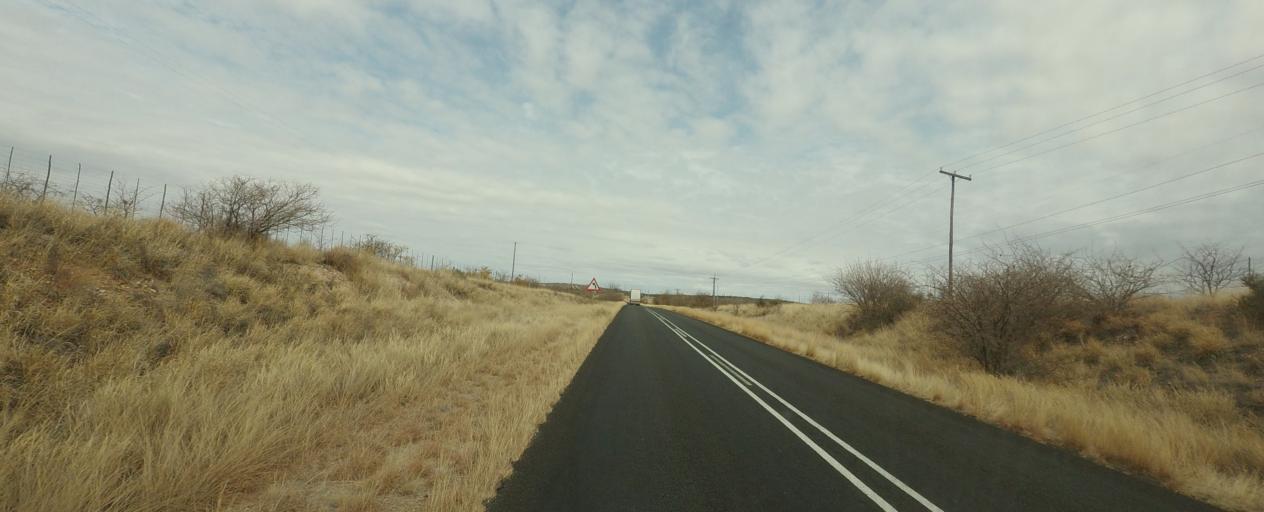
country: ZW
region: Matabeleland South
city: Beitbridge
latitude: -22.4296
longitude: 29.4257
